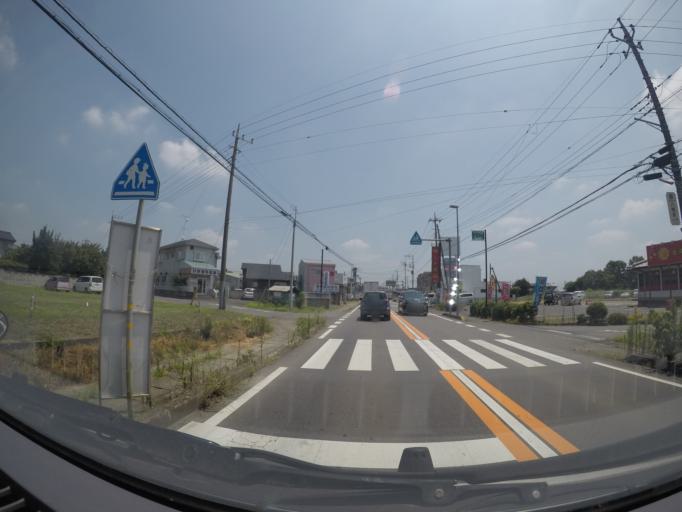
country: JP
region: Ibaraki
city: Ishige
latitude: 36.1898
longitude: 139.8863
